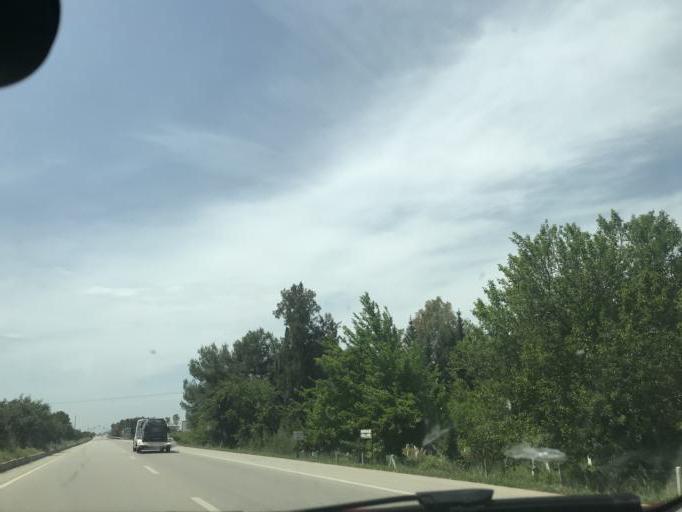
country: TR
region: Adana
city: Yakapinar
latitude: 36.9722
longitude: 35.5149
